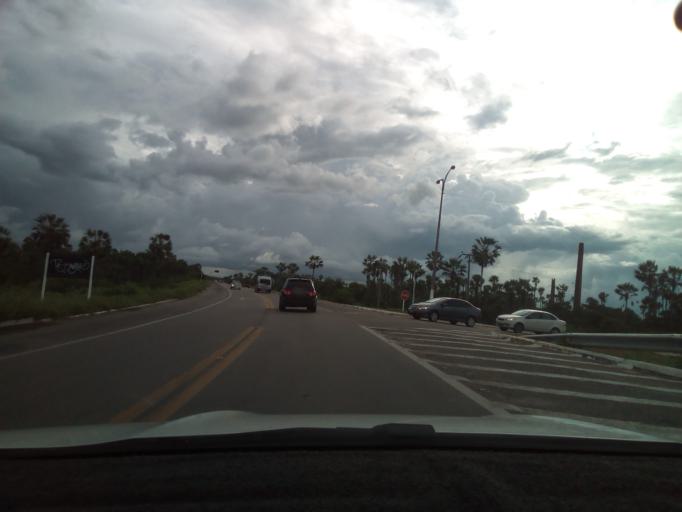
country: BR
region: Ceara
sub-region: Aracati
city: Aracati
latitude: -4.5687
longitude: -37.7515
